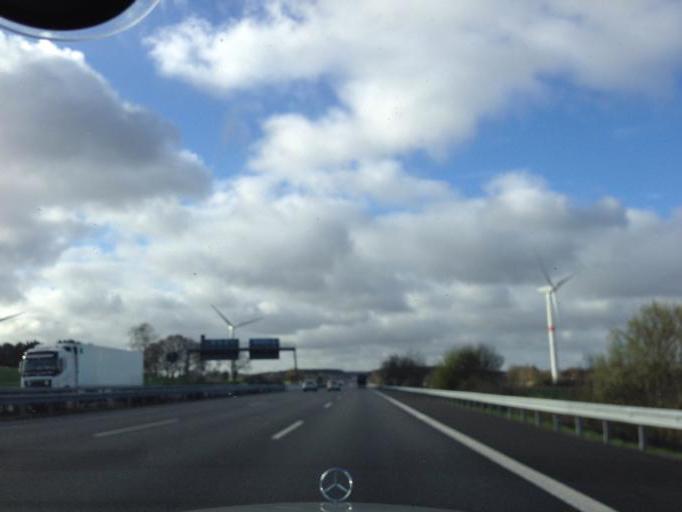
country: DE
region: Lower Saxony
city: Marxen
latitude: 53.3592
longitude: 10.0369
